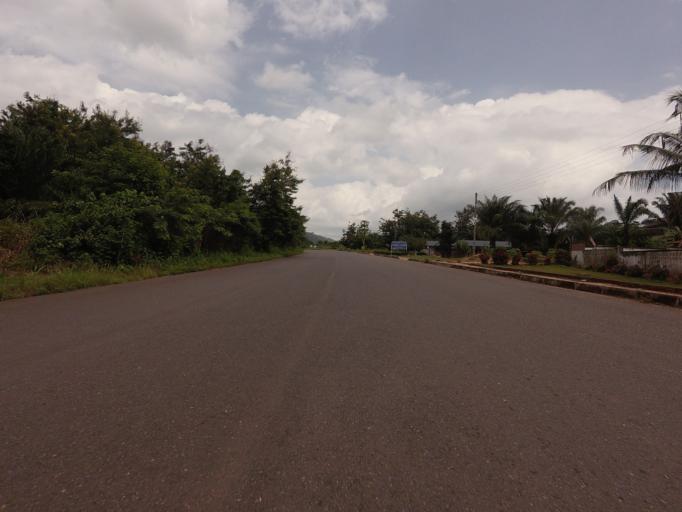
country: GH
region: Volta
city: Ho
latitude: 6.5211
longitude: 0.2201
